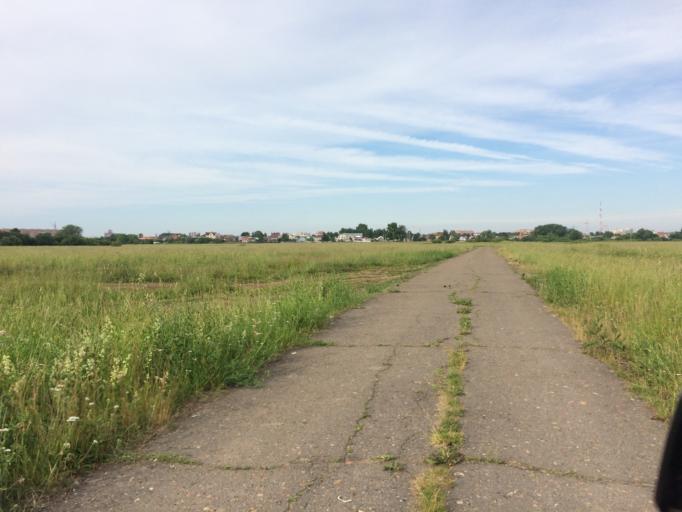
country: RU
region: Mariy-El
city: Yoshkar-Ola
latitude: 56.6554
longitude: 47.9224
